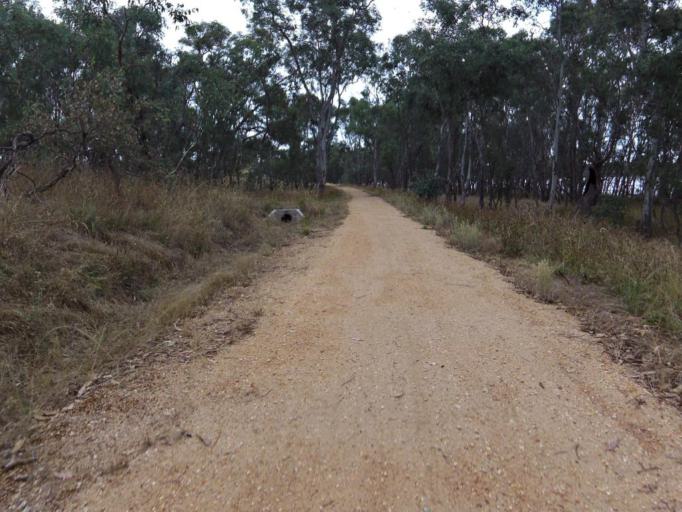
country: AU
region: Victoria
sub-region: Greater Bendigo
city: Kennington
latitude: -36.8656
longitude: 144.6230
